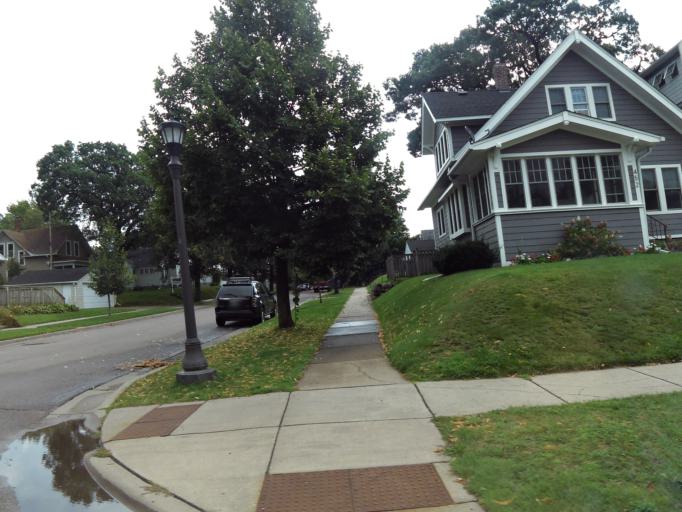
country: US
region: Minnesota
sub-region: Dakota County
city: Mendota Heights
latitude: 44.9278
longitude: -93.1568
